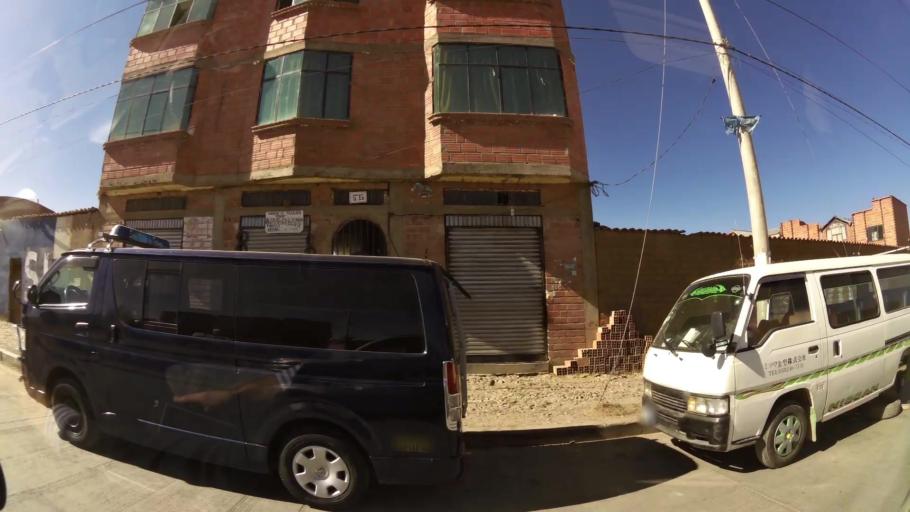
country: BO
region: La Paz
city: La Paz
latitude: -16.5352
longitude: -68.2188
